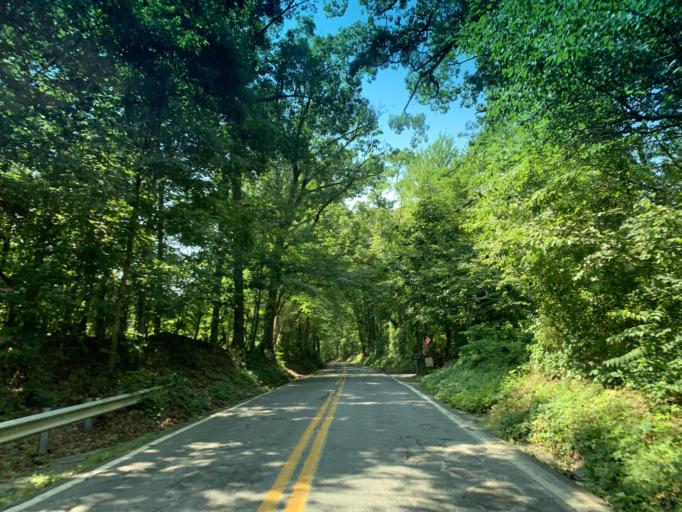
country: US
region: Maryland
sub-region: Frederick County
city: Urbana
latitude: 39.2516
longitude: -77.3826
